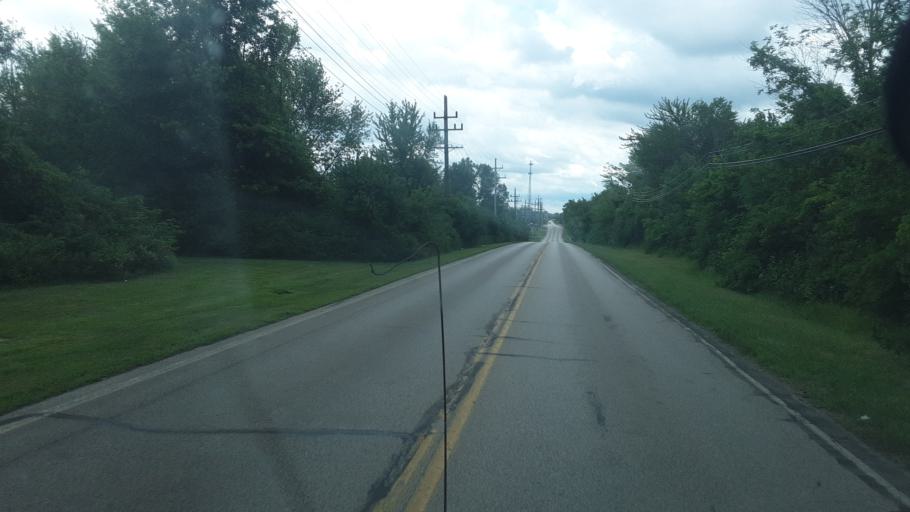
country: US
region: Ohio
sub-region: Ashtabula County
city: Edgewood
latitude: 41.8954
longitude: -80.7725
